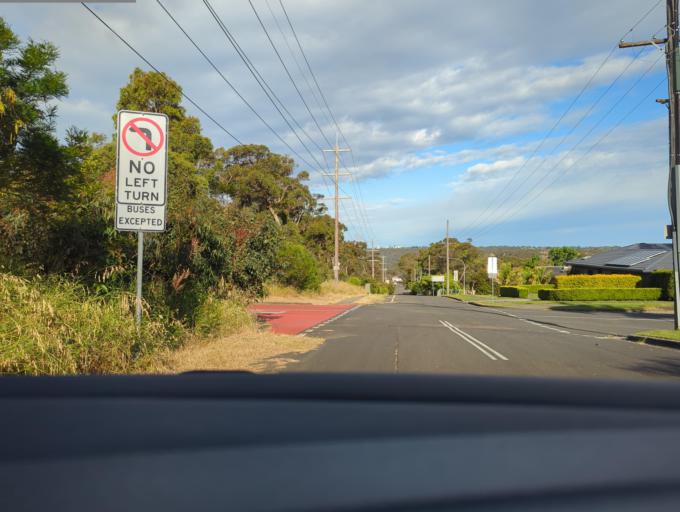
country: AU
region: New South Wales
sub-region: Sutherland Shire
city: Menai
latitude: -34.0246
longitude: 151.0133
